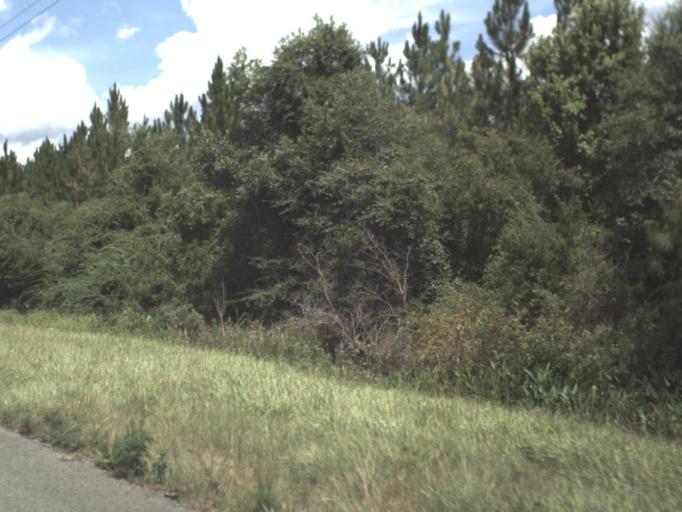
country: US
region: Florida
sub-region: Taylor County
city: Perry
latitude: 30.0888
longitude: -83.6749
